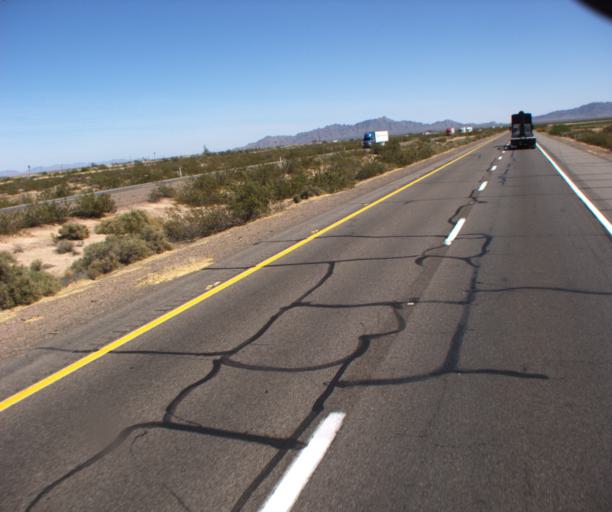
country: US
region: Arizona
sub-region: Yuma County
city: Wellton
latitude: 32.6996
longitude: -113.9124
